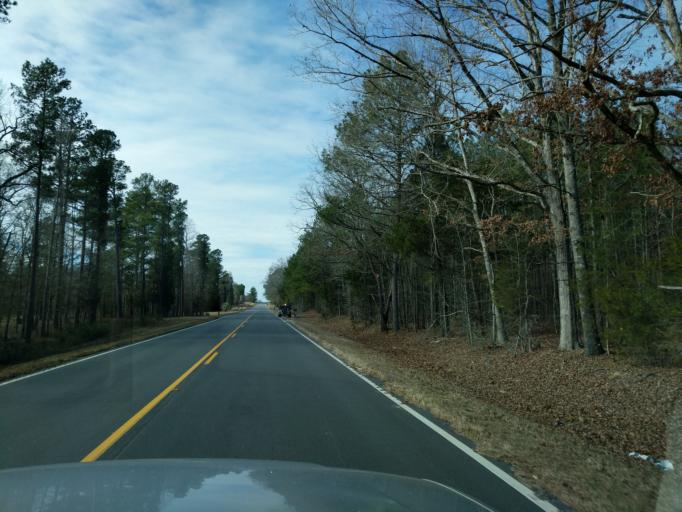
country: US
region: South Carolina
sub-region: Edgefield County
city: Edgefield
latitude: 33.9378
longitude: -81.9420
